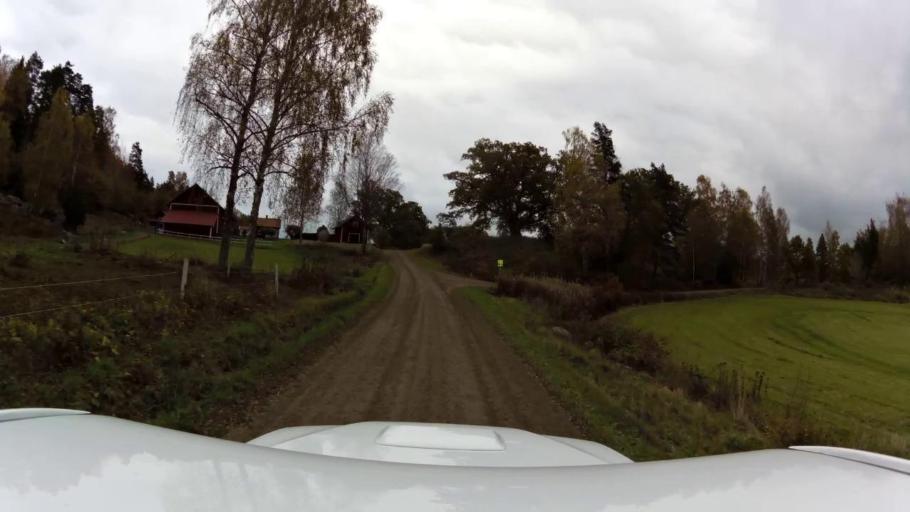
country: SE
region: OEstergoetland
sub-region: Linkopings Kommun
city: Ljungsbro
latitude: 58.5761
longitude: 15.4182
